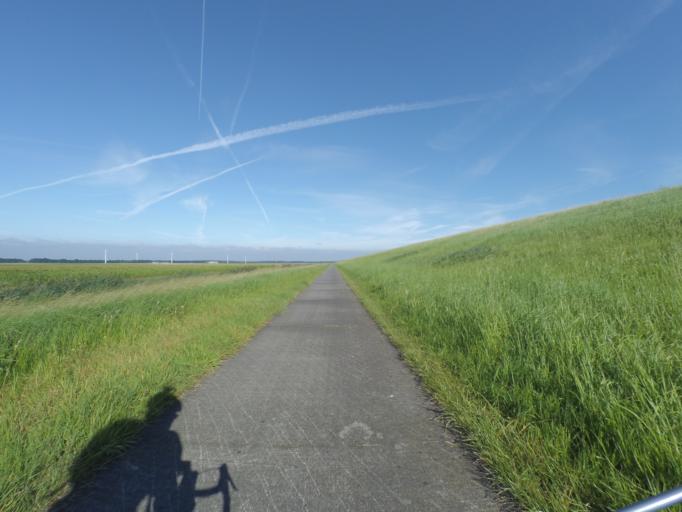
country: NL
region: Flevoland
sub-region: Gemeente Lelystad
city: Lelystad
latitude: 52.4233
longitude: 5.4700
